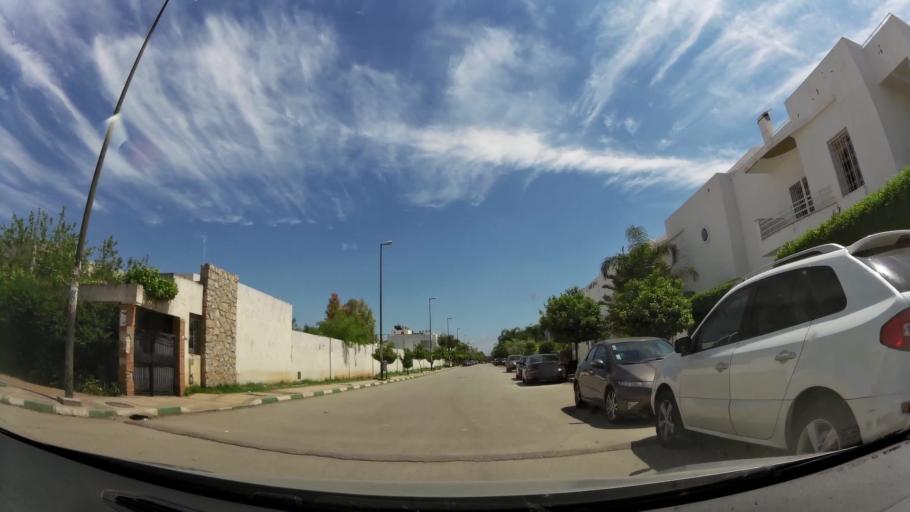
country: MA
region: Fes-Boulemane
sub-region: Fes
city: Fes
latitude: 34.0081
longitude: -4.9910
